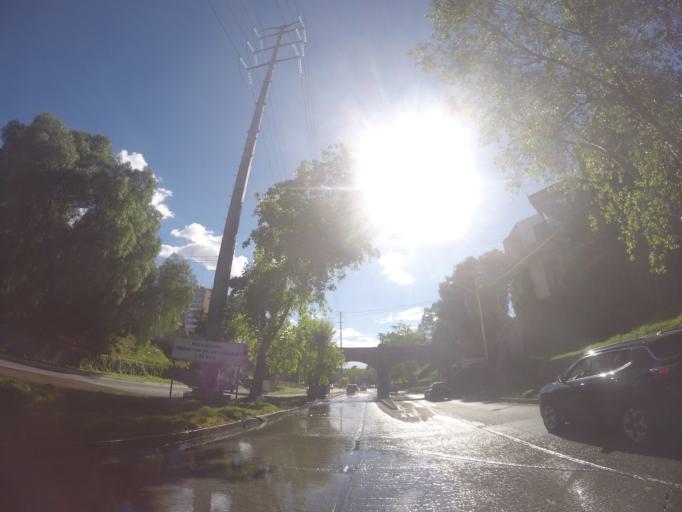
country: MX
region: San Luis Potosi
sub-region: San Luis Potosi
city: San Luis Potosi
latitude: 22.1635
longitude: -100.9927
